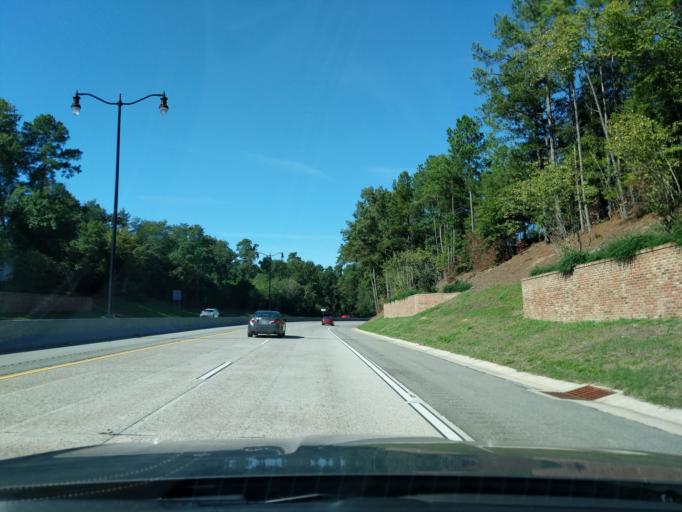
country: US
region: Georgia
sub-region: Richmond County
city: Augusta
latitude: 33.4874
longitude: -82.0074
